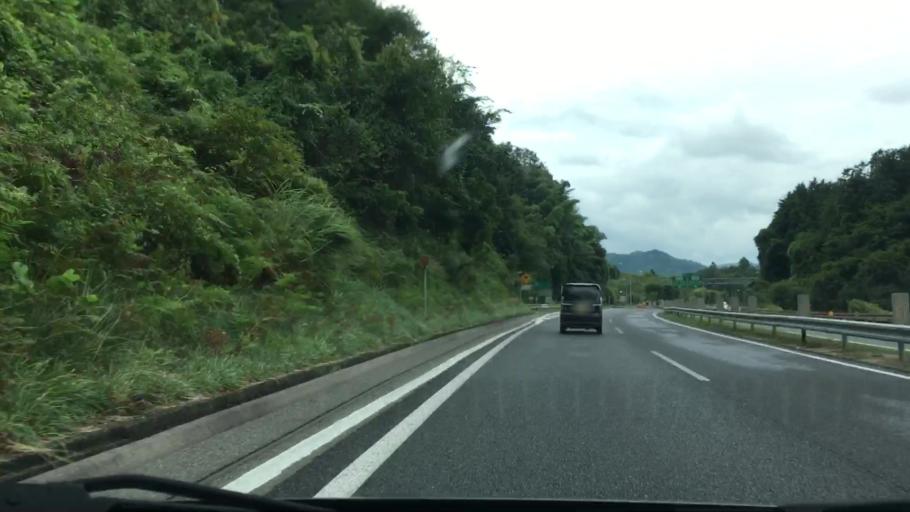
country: JP
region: Okayama
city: Tsuyama
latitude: 35.0569
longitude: 133.8227
